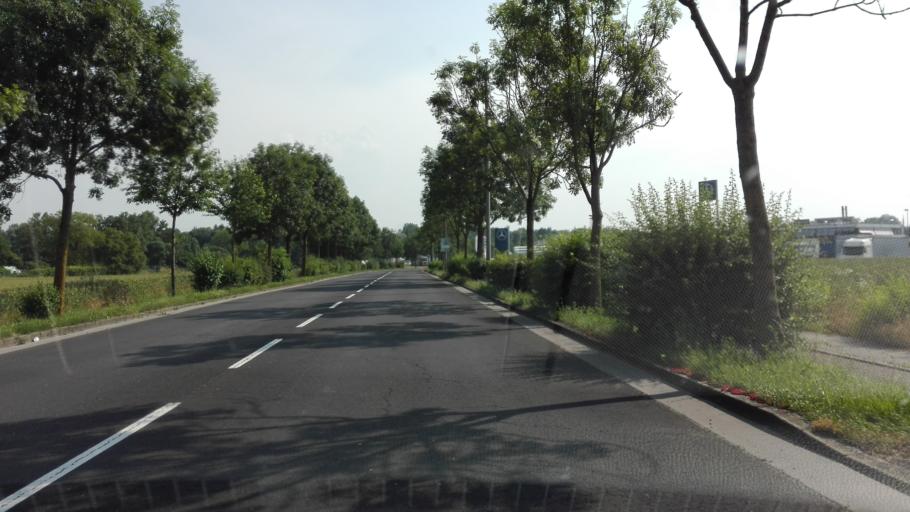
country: AT
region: Upper Austria
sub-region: Politischer Bezirk Linz-Land
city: Ansfelden
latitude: 48.2401
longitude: 14.2850
